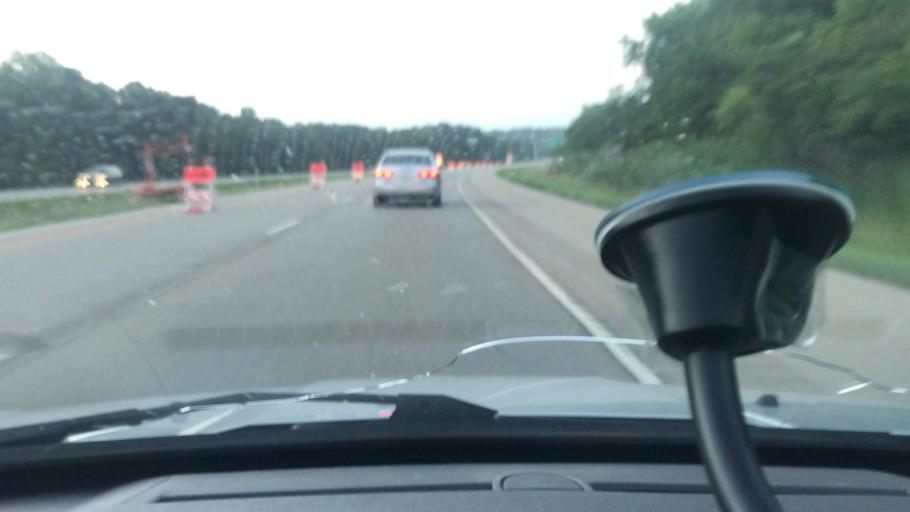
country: US
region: Illinois
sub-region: Peoria County
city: Bellevue
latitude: 40.7232
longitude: -89.6762
